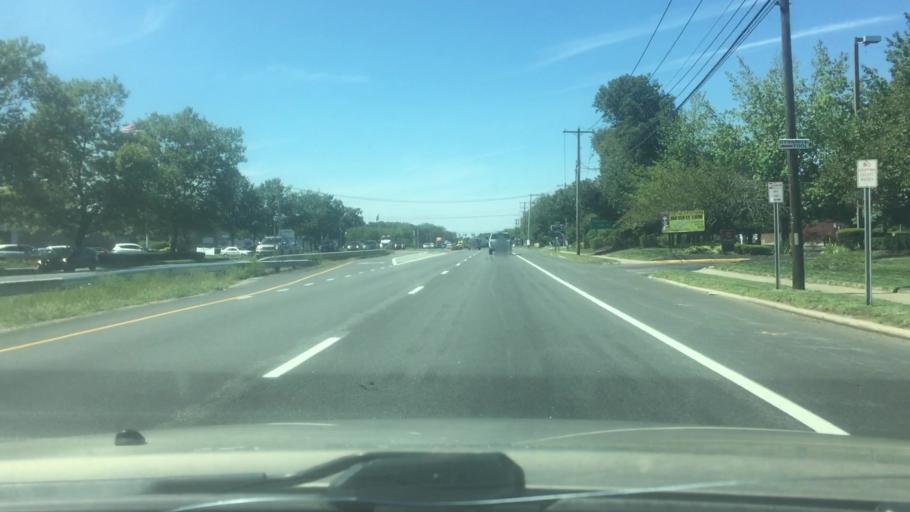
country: US
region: New York
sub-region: Suffolk County
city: Bohemia
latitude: 40.7848
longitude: -73.1096
